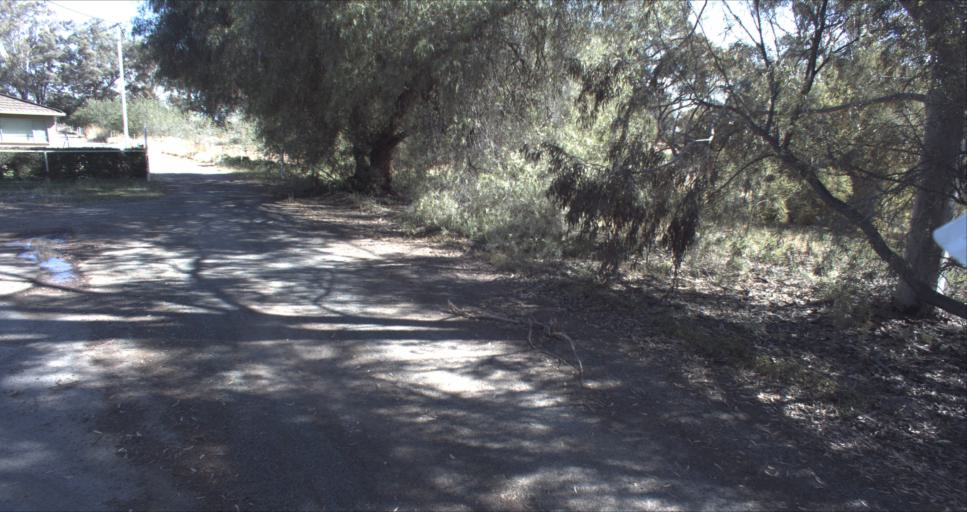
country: AU
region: New South Wales
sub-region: Leeton
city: Leeton
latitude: -34.5599
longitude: 146.3885
